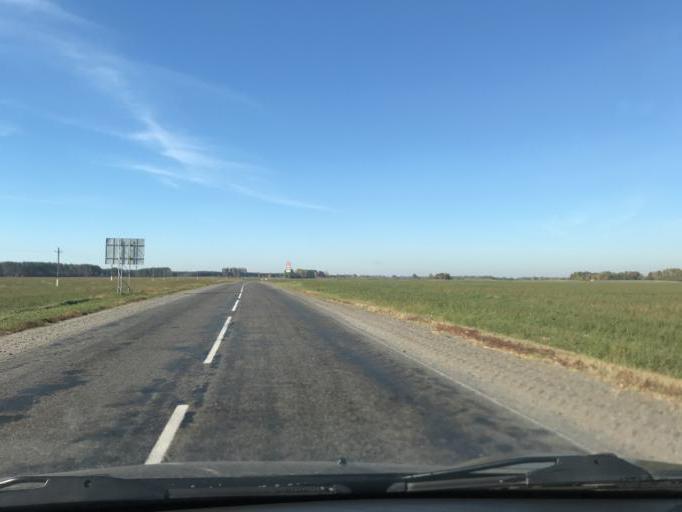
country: BY
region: Gomel
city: Brahin
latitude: 51.6686
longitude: 30.4169
